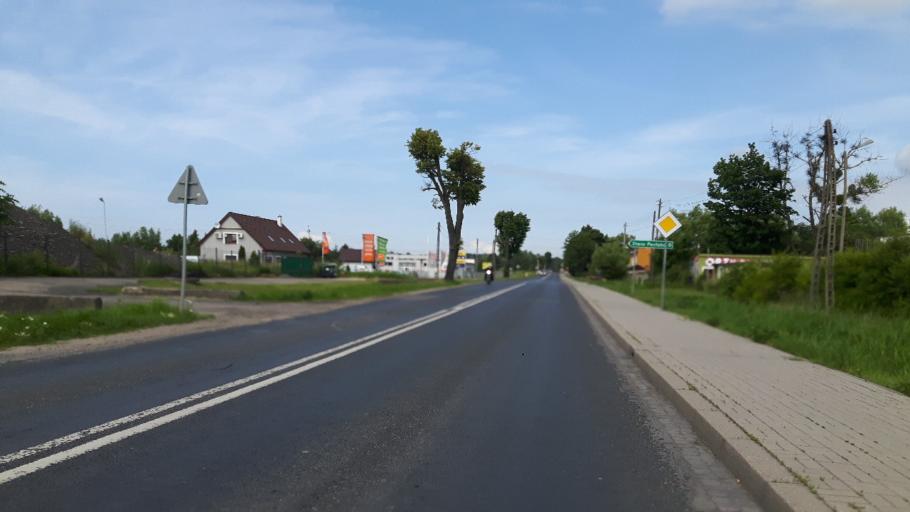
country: PL
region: Warmian-Masurian Voivodeship
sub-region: Powiat braniewski
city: Braniewo
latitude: 54.3928
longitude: 19.8376
